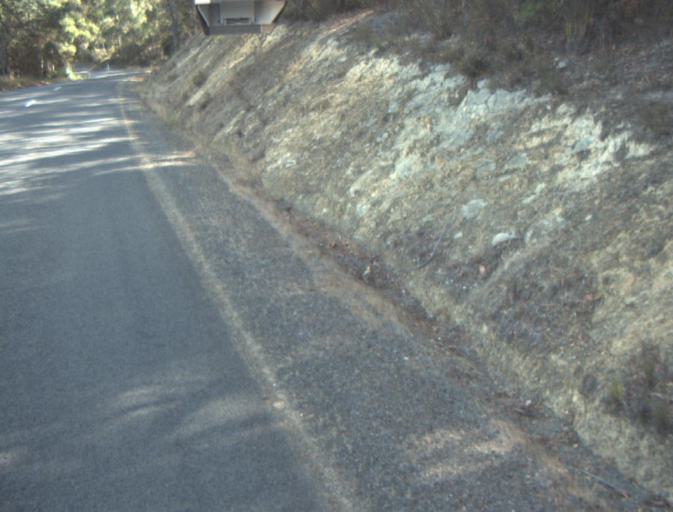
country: AU
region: Tasmania
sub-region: Dorset
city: Bridport
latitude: -41.1548
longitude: 147.2384
